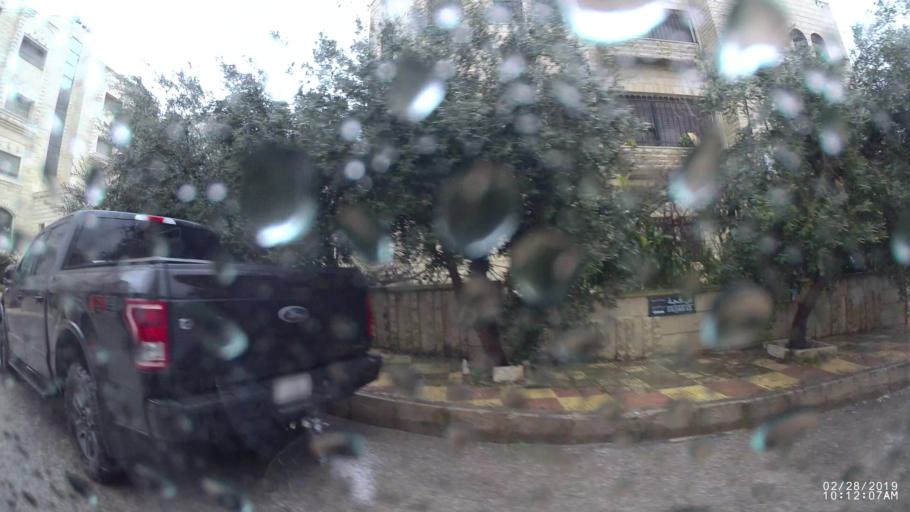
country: JO
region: Amman
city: Al Jubayhah
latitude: 32.0125
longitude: 35.8866
